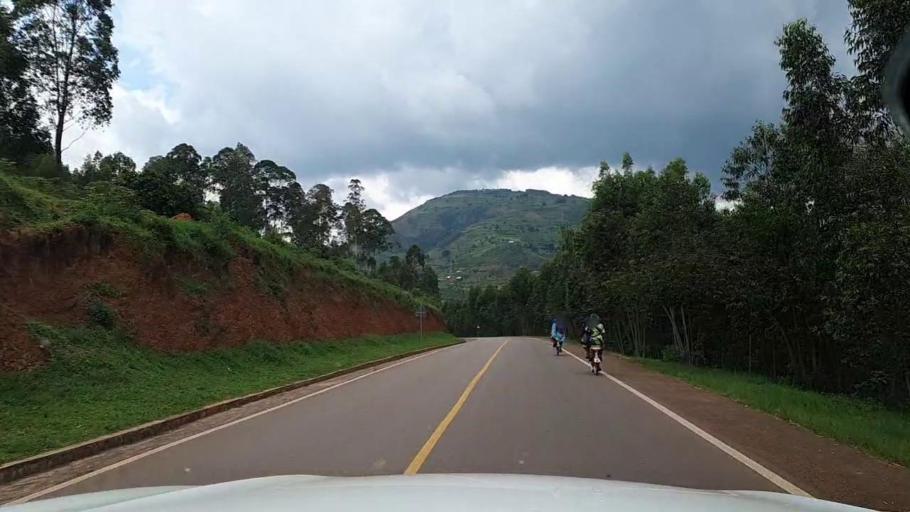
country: RW
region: Kigali
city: Kigali
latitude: -1.7734
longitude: 30.1258
